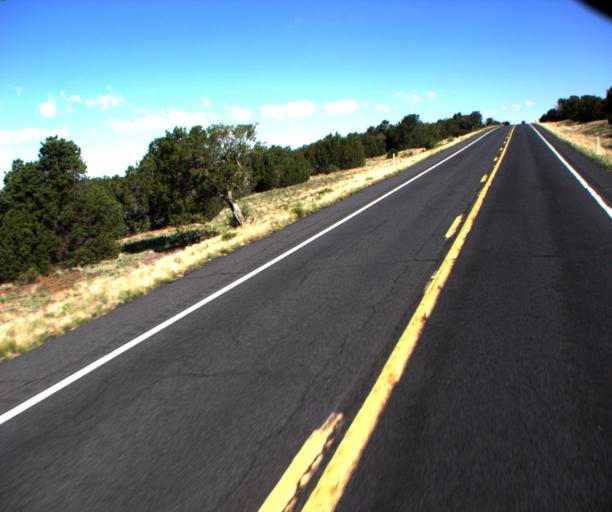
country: US
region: Arizona
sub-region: Coconino County
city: Williams
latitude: 35.3934
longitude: -112.1673
